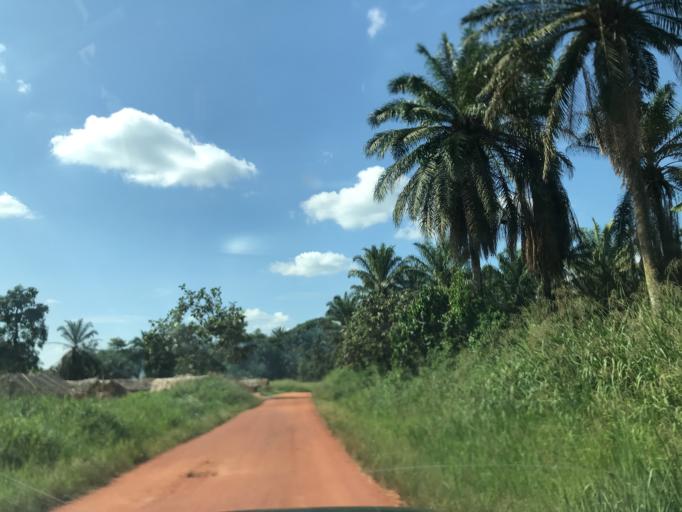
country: CD
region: Eastern Province
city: Kisangani
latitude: 1.2014
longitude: 25.2576
